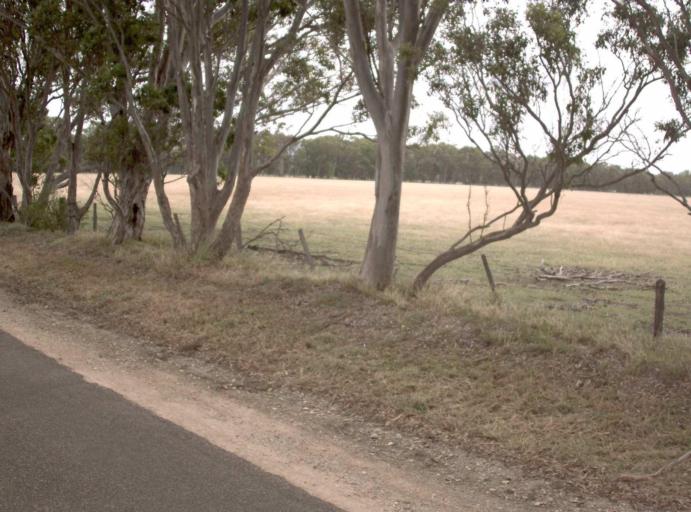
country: AU
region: Victoria
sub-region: Wellington
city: Sale
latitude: -37.8727
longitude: 147.0668
